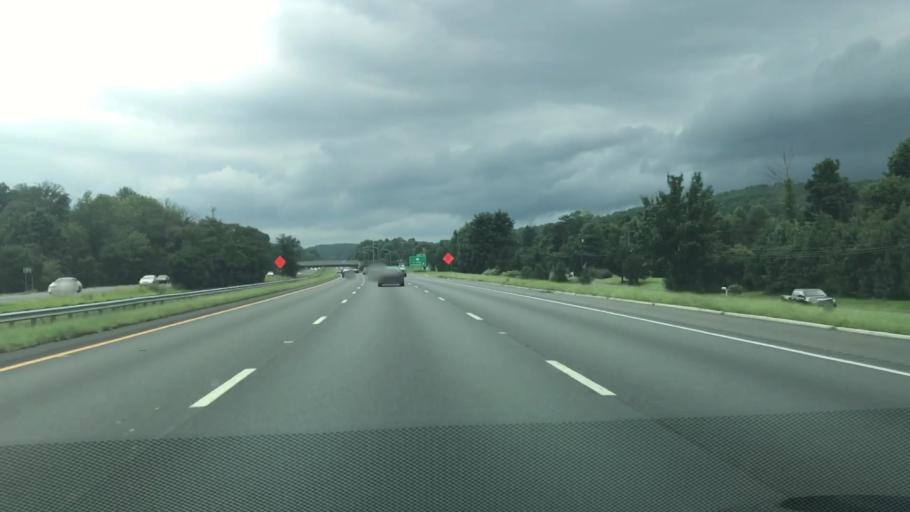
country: US
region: New Jersey
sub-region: Hunterdon County
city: Hampton
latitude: 40.6423
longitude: -74.9907
